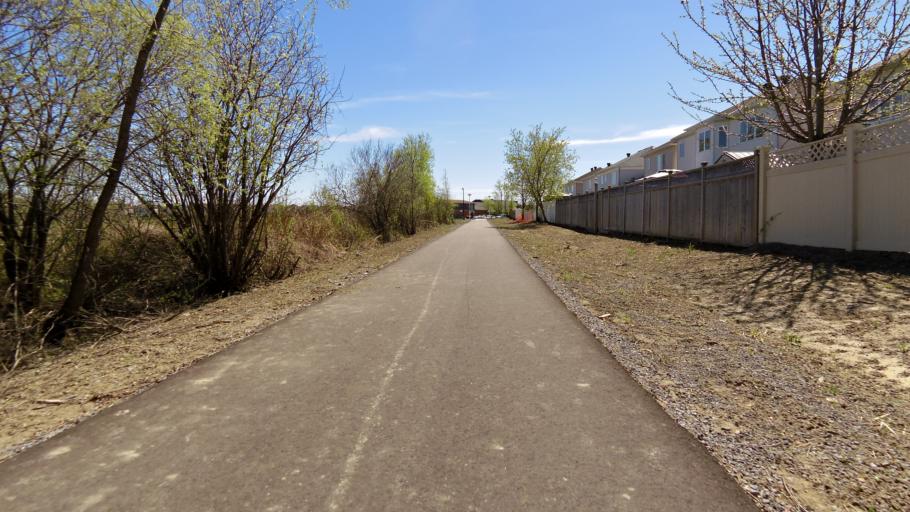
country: CA
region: Ontario
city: Clarence-Rockland
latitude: 45.4600
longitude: -75.4680
